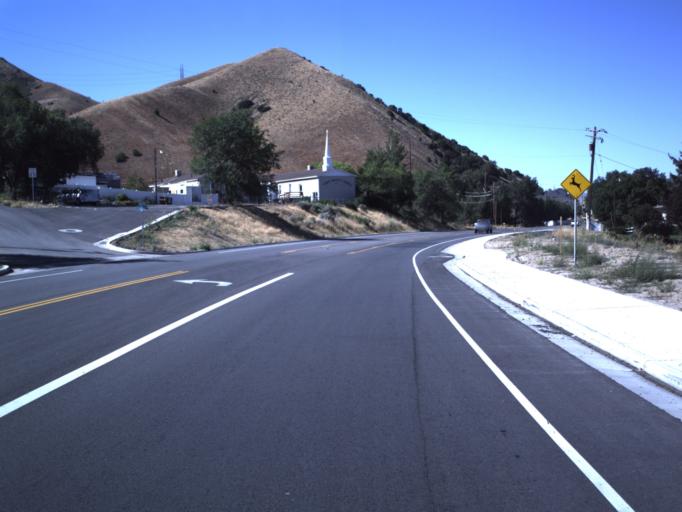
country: US
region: Utah
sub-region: Tooele County
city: Tooele
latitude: 40.5193
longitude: -112.2998
